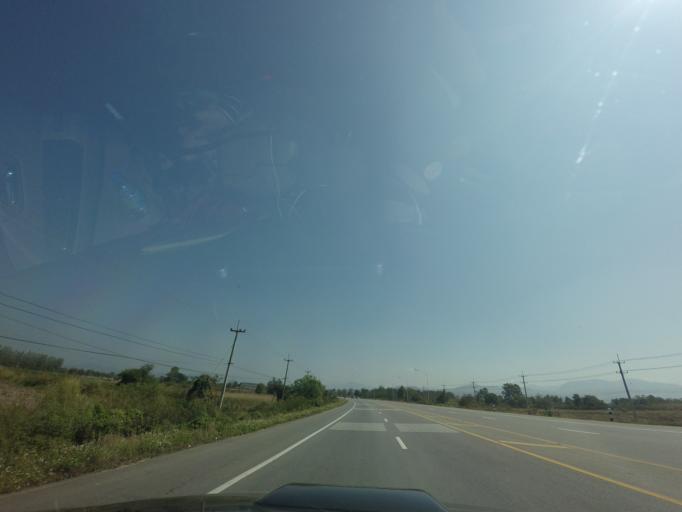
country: TH
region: Chiang Mai
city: San Kamphaeng
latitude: 18.7110
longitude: 99.1310
